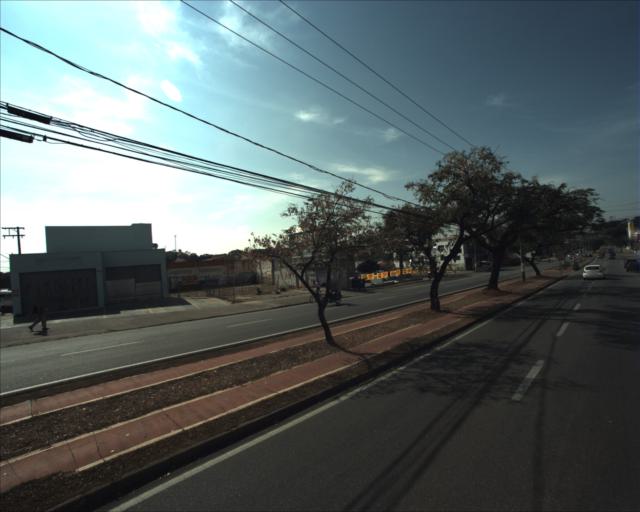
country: BR
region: Sao Paulo
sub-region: Sorocaba
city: Sorocaba
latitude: -23.4820
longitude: -47.4772
